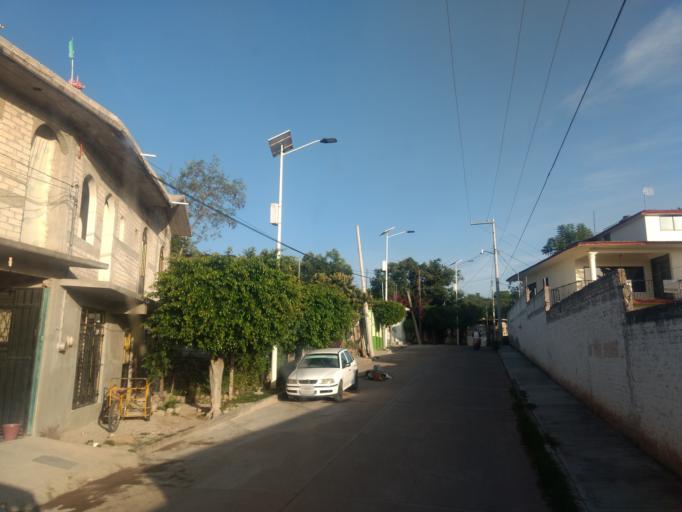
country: MX
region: Oaxaca
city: Ciudad de Huajuapam de Leon
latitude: 17.8160
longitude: -97.7884
